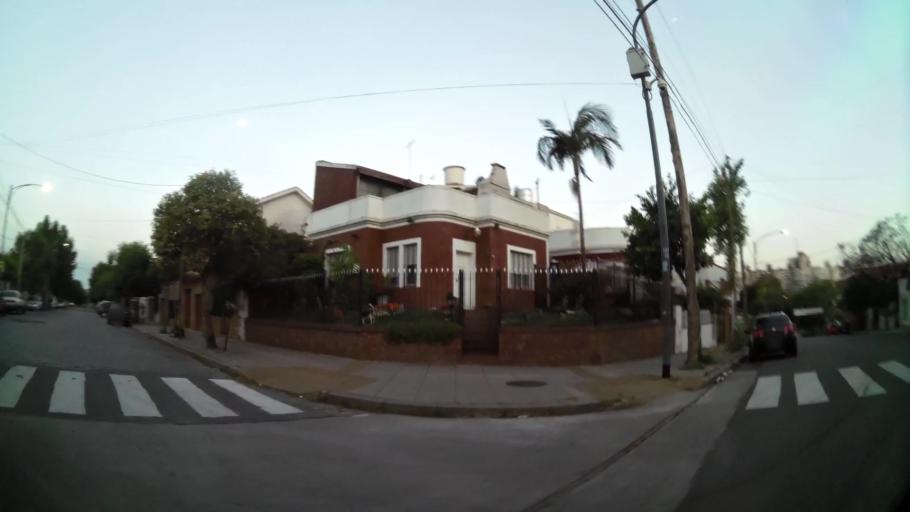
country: AR
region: Buenos Aires F.D.
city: Villa Lugano
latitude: -34.6803
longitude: -58.4714
